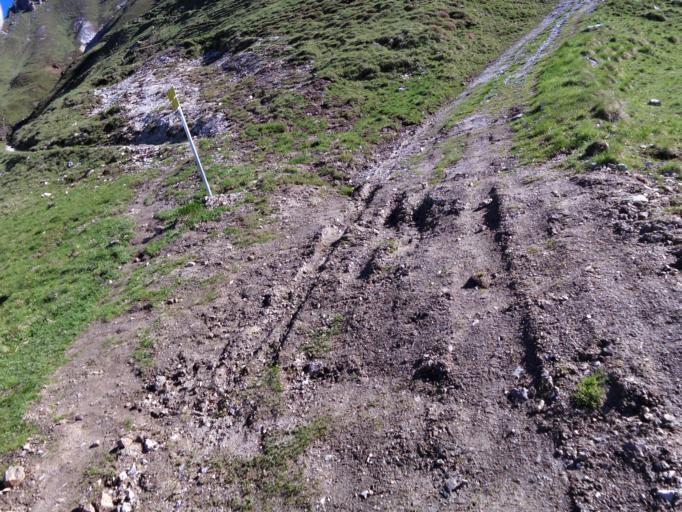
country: AT
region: Tyrol
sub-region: Politischer Bezirk Innsbruck Land
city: Neustift im Stubaital
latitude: 47.1277
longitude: 11.2794
